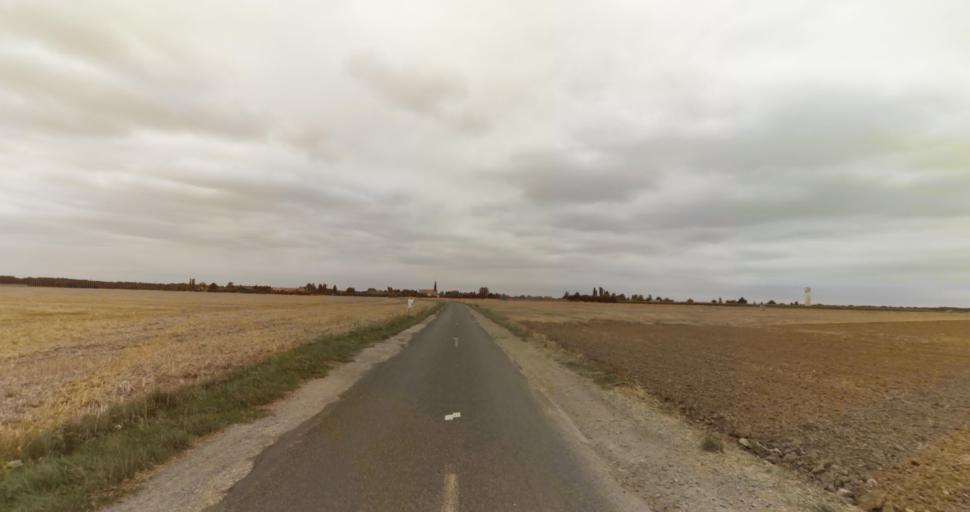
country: FR
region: Haute-Normandie
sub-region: Departement de l'Eure
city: La Couture-Boussey
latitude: 48.9141
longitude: 1.3407
